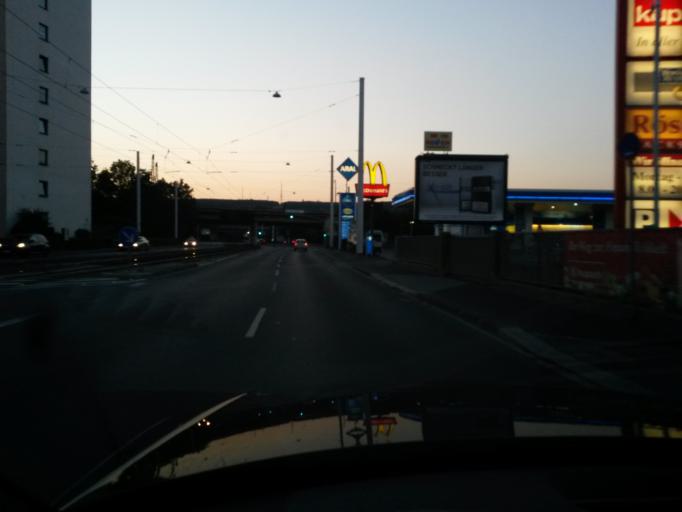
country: DE
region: Bavaria
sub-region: Regierungsbezirk Unterfranken
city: Wuerzburg
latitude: 49.7678
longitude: 9.9410
